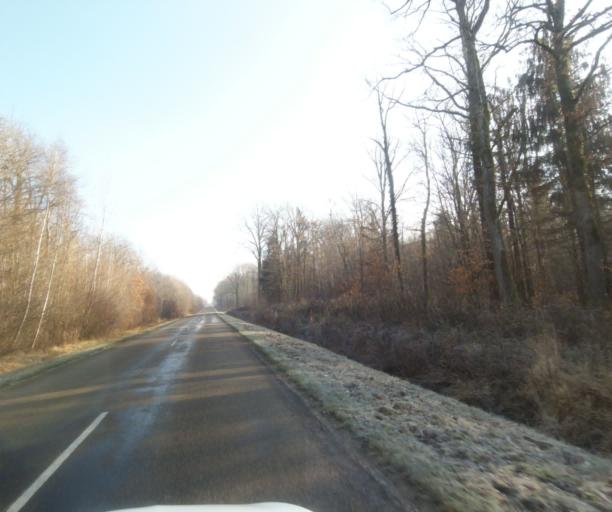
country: FR
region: Champagne-Ardenne
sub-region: Departement de la Haute-Marne
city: Laneuville-a-Remy
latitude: 48.4937
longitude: 4.9010
